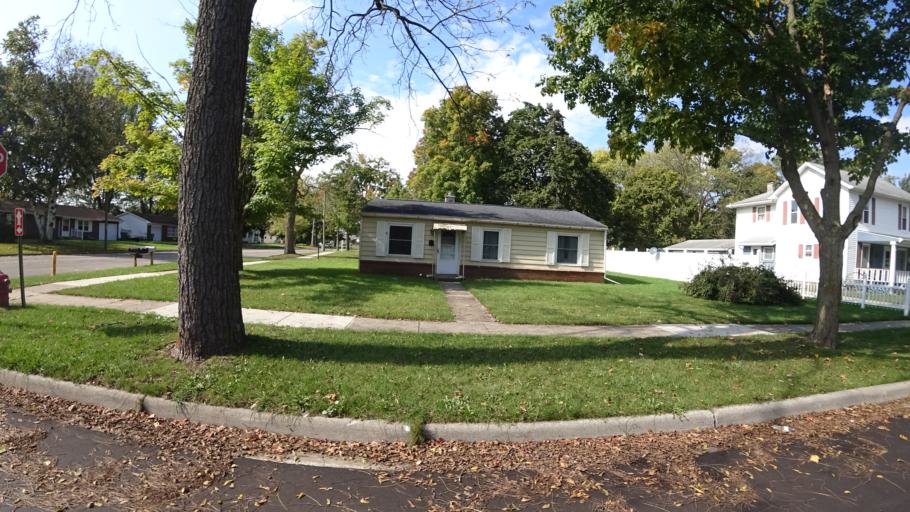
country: US
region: Michigan
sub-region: Saint Joseph County
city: Three Rivers
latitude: 41.9402
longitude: -85.6431
